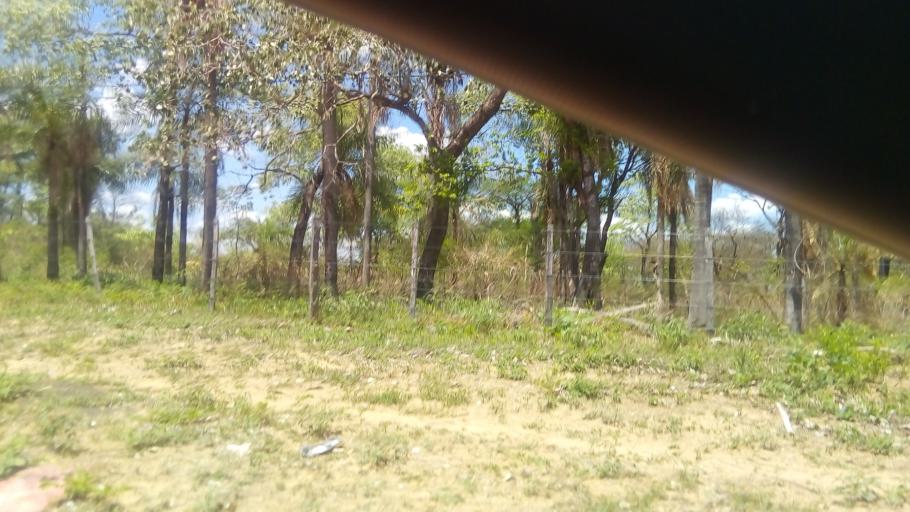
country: PY
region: Cordillera
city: Arroyos y Esteros
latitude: -24.9964
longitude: -57.2162
